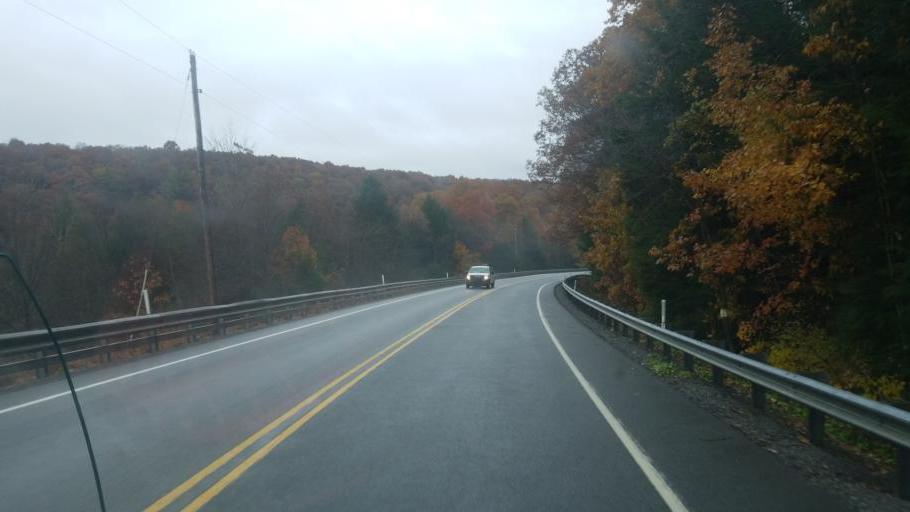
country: US
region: Pennsylvania
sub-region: Clearfield County
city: Shiloh
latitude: 41.1180
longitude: -78.1555
